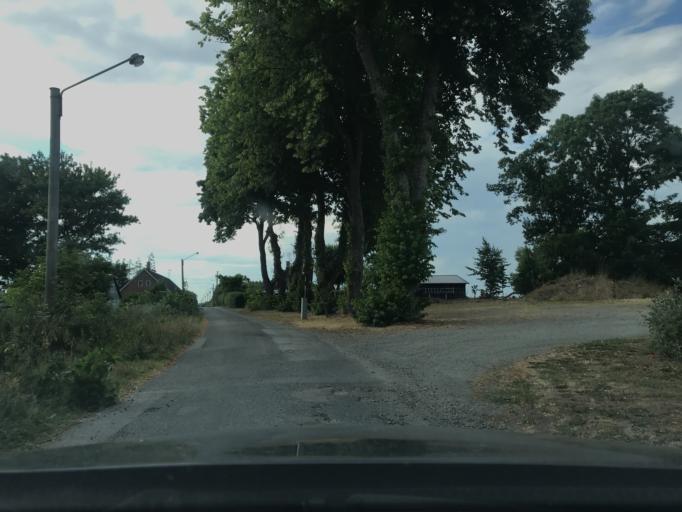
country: SE
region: Skane
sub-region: Simrishamns Kommun
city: Kivik
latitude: 55.5262
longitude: 14.1656
